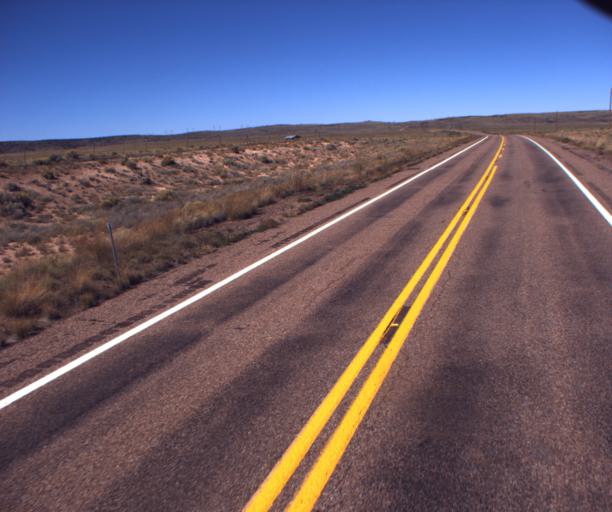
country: US
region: Arizona
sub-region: Apache County
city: Saint Johns
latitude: 34.5333
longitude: -109.4619
